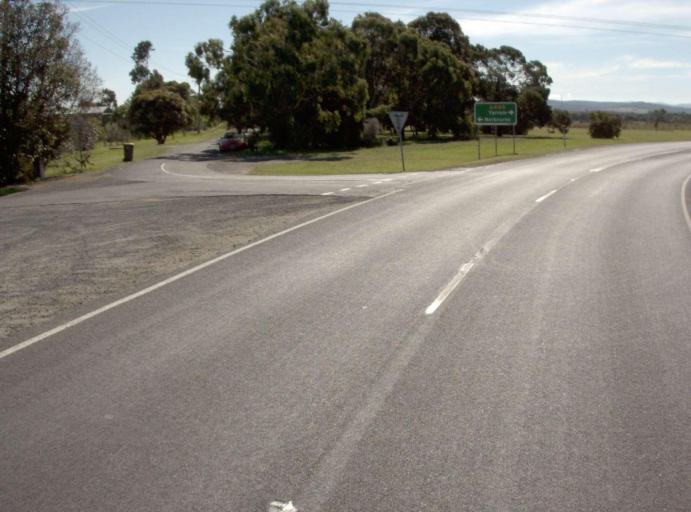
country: AU
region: Victoria
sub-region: Latrobe
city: Traralgon
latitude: -38.6212
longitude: 146.6694
